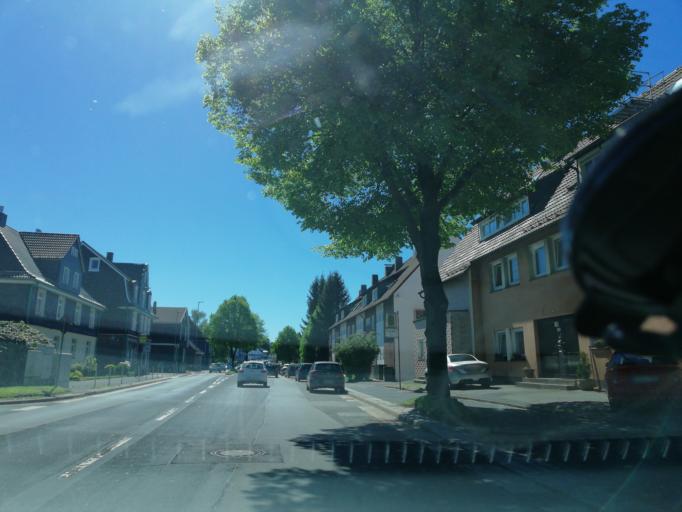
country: DE
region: North Rhine-Westphalia
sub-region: Regierungsbezirk Dusseldorf
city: Remscheid
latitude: 51.2092
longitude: 7.2426
